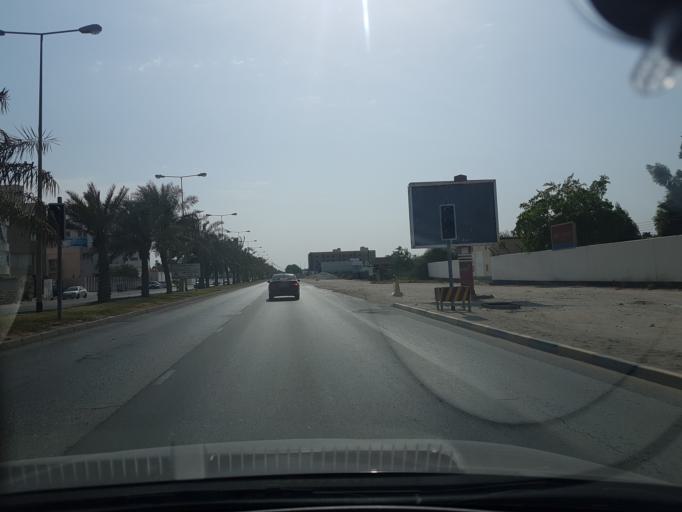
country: BH
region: Manama
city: Jidd Hafs
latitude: 26.2190
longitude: 50.4897
